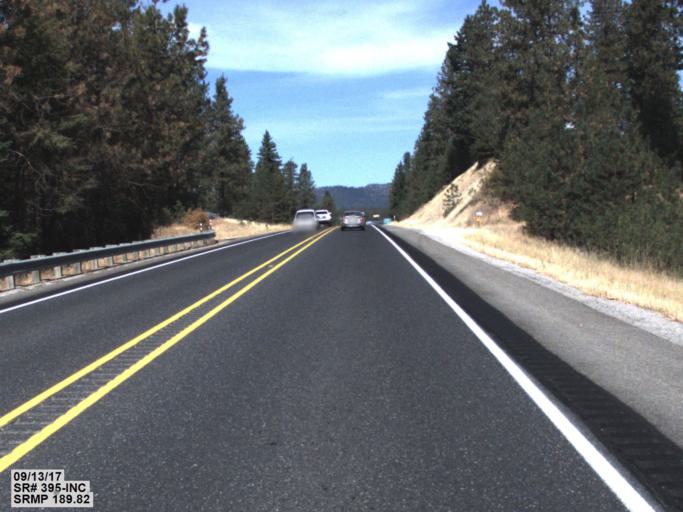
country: US
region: Washington
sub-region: Spokane County
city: Deer Park
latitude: 48.0504
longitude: -117.6124
